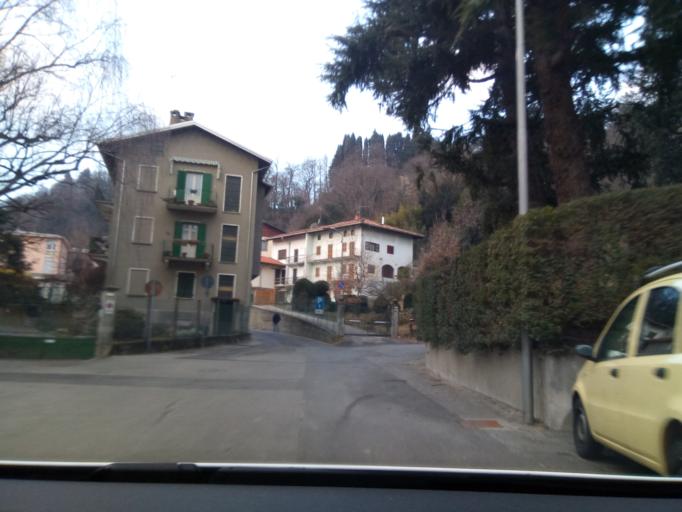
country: IT
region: Piedmont
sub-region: Provincia di Torino
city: Ivrea
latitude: 45.4548
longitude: 7.8777
